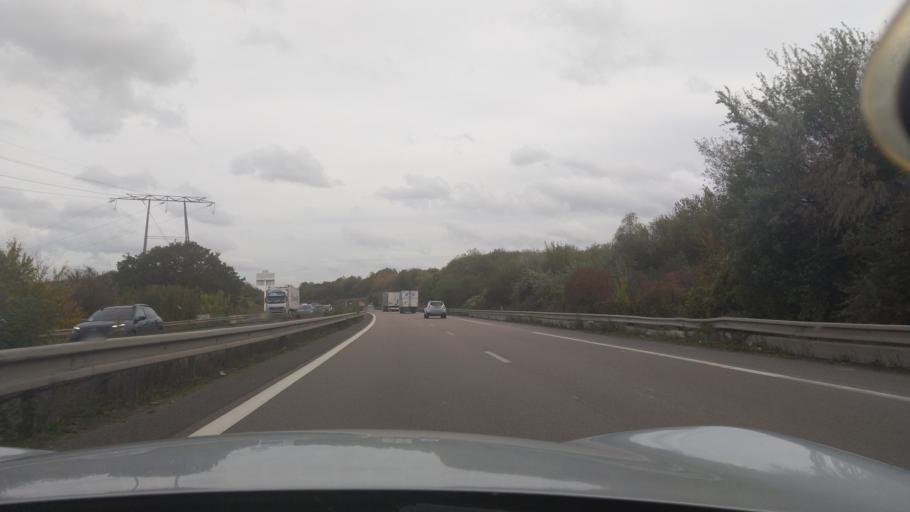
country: FR
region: Ile-de-France
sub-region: Departement du Val-d'Oise
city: Louvres
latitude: 49.0346
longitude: 2.4880
